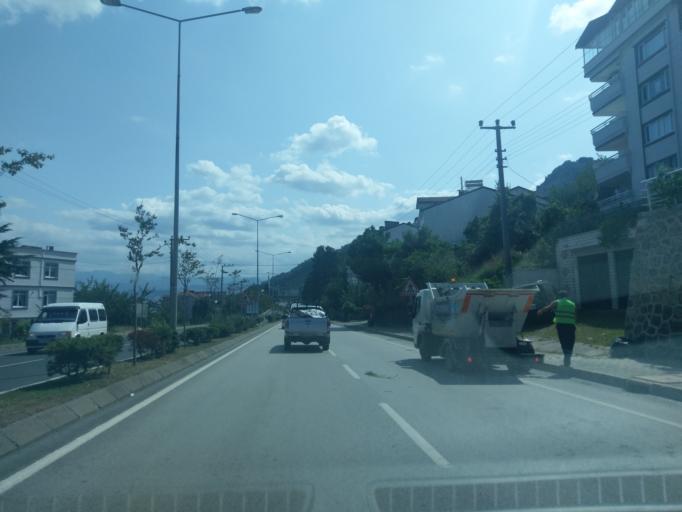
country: TR
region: Ordu
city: Ordu
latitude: 41.0077
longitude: 37.8690
